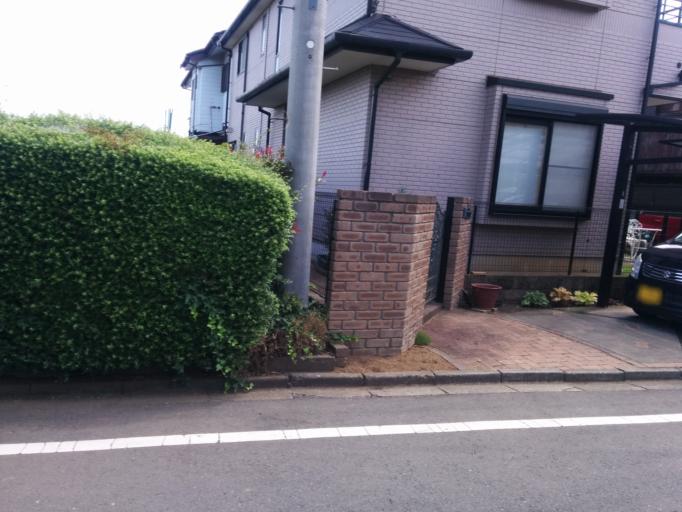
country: JP
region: Tokyo
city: Higashimurayama-shi
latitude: 35.7569
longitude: 139.4839
